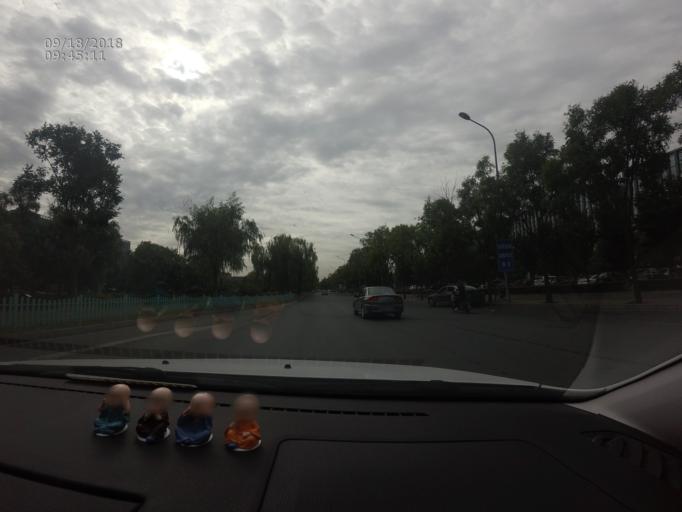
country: CN
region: Beijing
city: Xibeiwang
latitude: 40.0715
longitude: 116.2376
